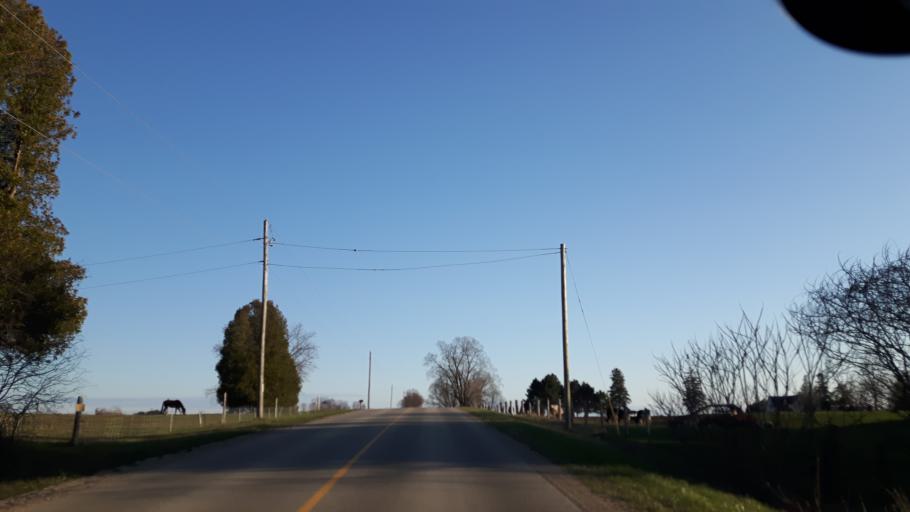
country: CA
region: Ontario
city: Goderich
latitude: 43.6671
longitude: -81.6847
